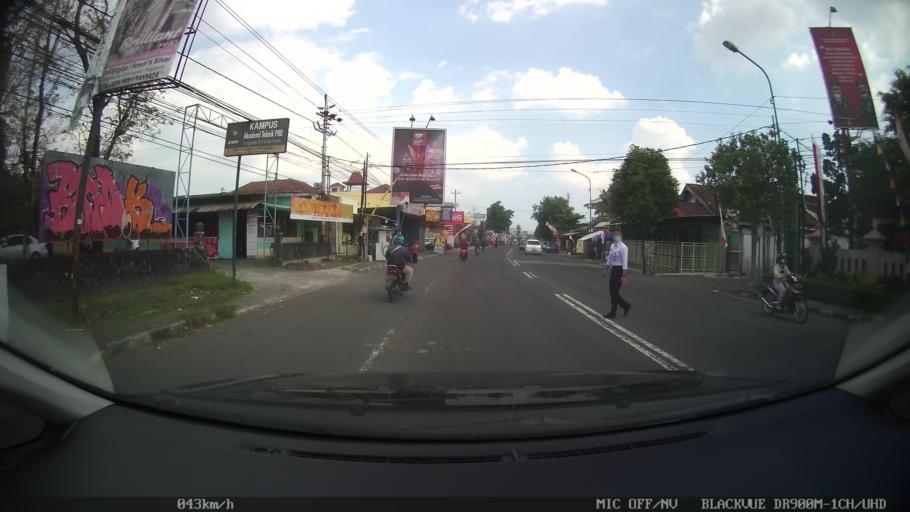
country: ID
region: Daerah Istimewa Yogyakarta
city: Yogyakarta
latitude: -7.8169
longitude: 110.4021
